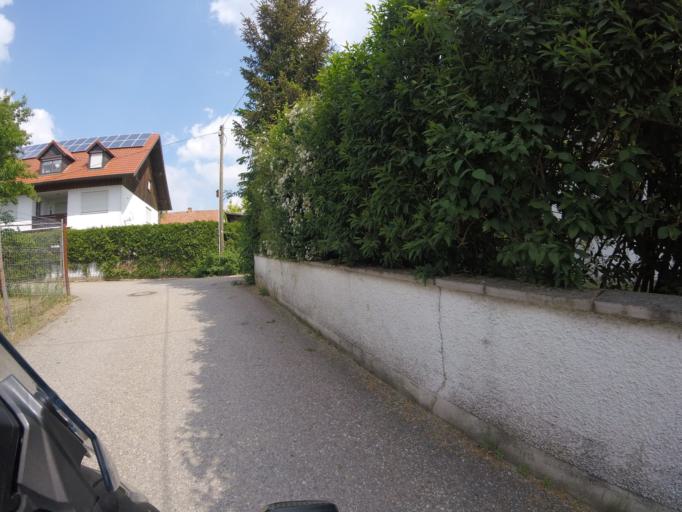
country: DE
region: Bavaria
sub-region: Upper Bavaria
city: Schweitenkirchen
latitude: 48.5112
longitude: 11.6391
